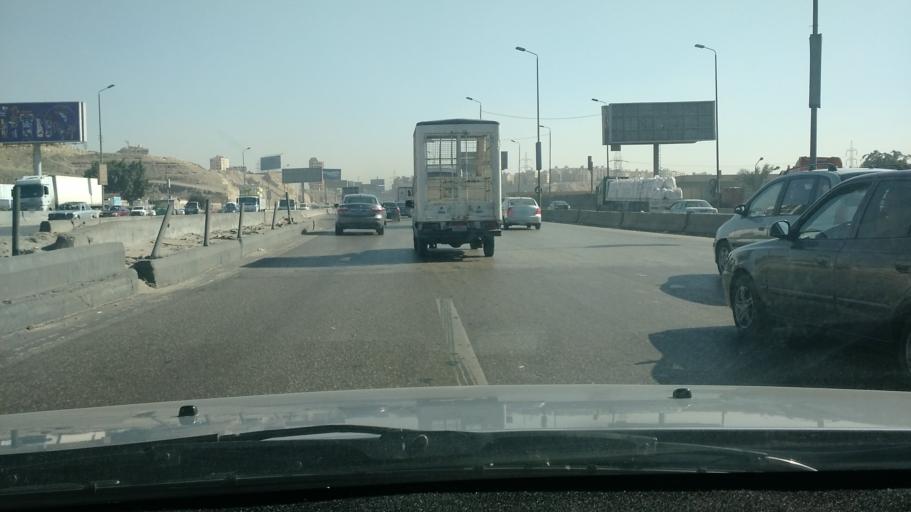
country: EG
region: Muhafazat al Qahirah
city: Cairo
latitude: 29.9922
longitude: 31.2919
